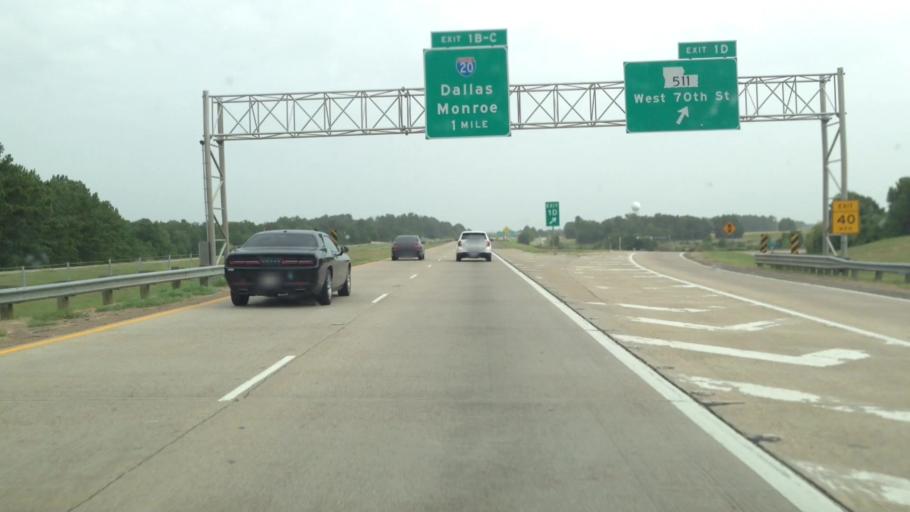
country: US
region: Louisiana
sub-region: Caddo Parish
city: Shreveport
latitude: 32.4388
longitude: -93.8412
